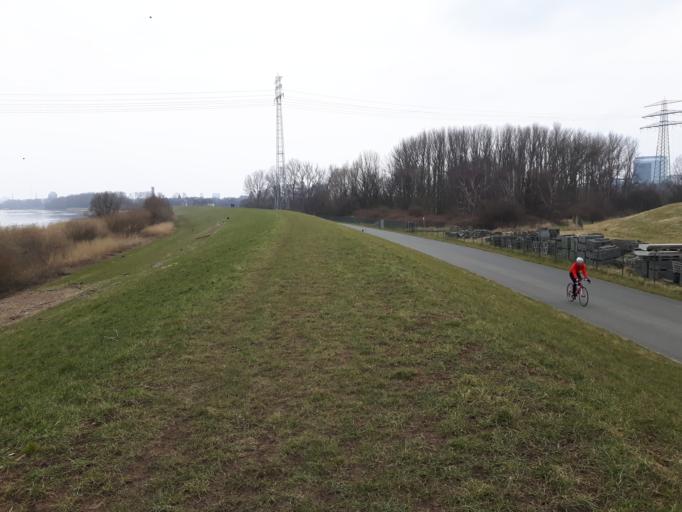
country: DE
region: Hamburg
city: Rothenburgsort
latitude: 53.5176
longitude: 10.0604
